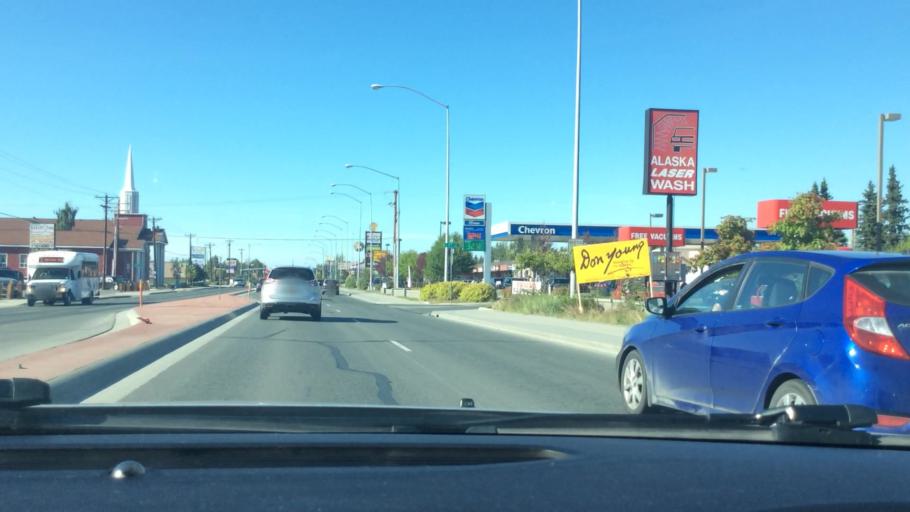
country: US
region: Alaska
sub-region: Anchorage Municipality
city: Elmendorf Air Force Base
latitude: 61.2175
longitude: -149.7334
